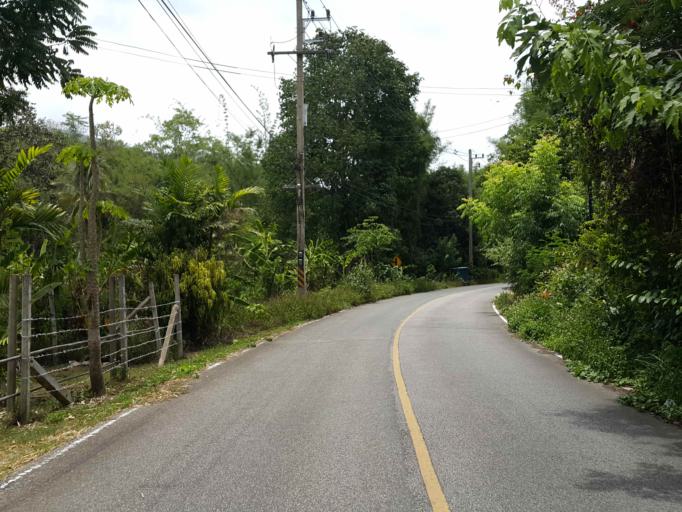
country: TH
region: Chiang Mai
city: Hang Dong
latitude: 18.7568
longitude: 98.9067
